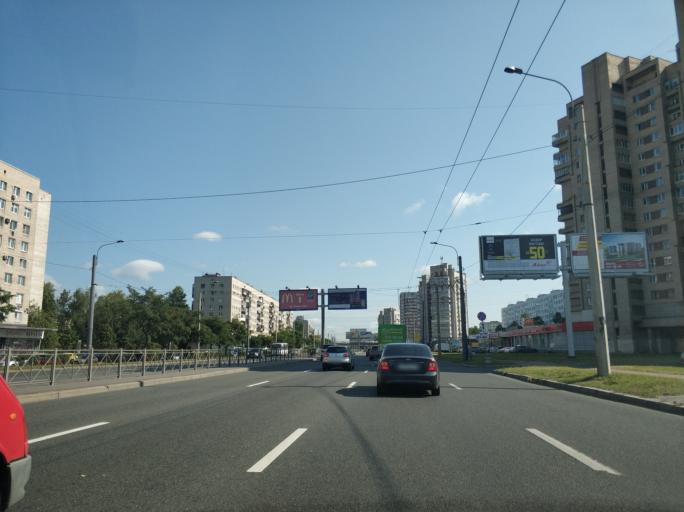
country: RU
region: St.-Petersburg
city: Kupchino
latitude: 59.8549
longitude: 30.3717
